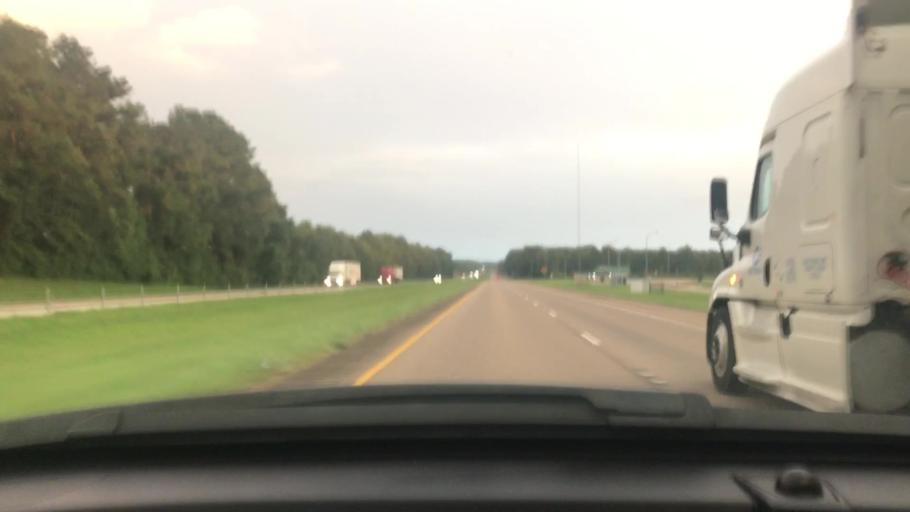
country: US
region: Louisiana
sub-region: Tangipahoa Parish
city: Kentwood
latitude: 30.8959
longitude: -90.5278
